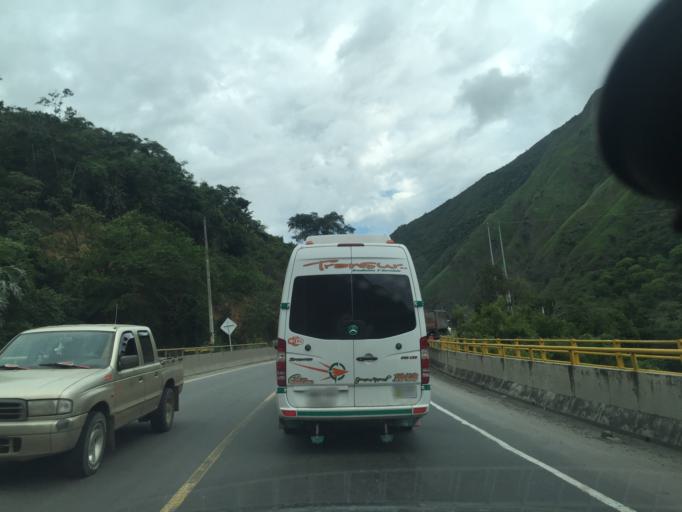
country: CO
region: Valle del Cauca
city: Dagua
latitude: 3.7779
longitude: -76.7030
